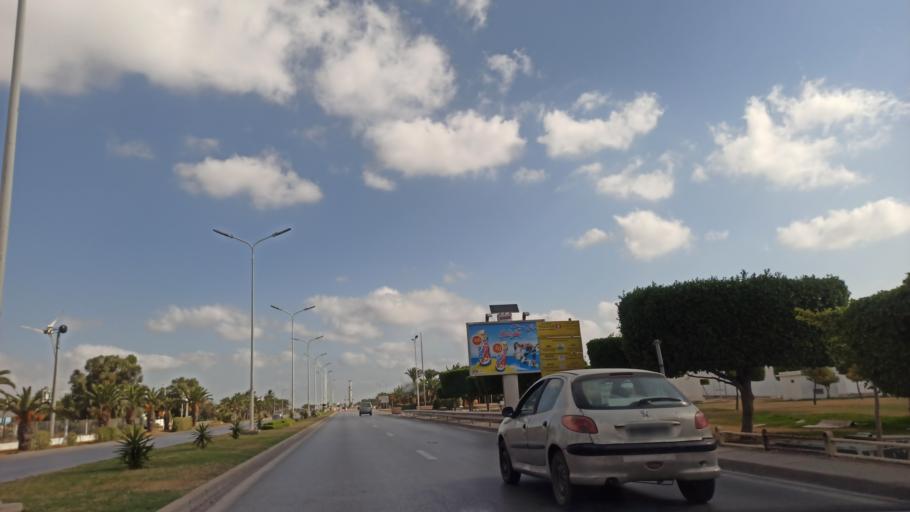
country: TN
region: Ariana
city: Ariana
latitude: 36.8374
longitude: 10.2134
